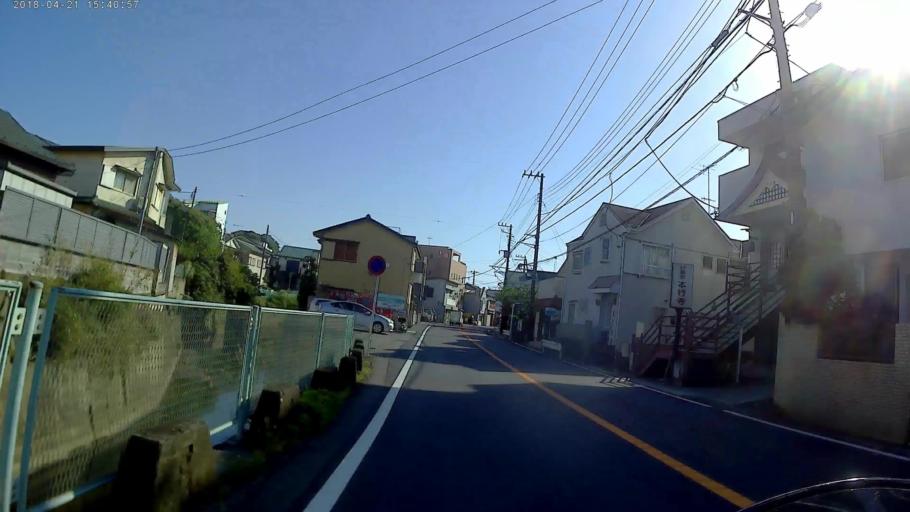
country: JP
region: Kanagawa
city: Fujisawa
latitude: 35.3095
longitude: 139.4938
